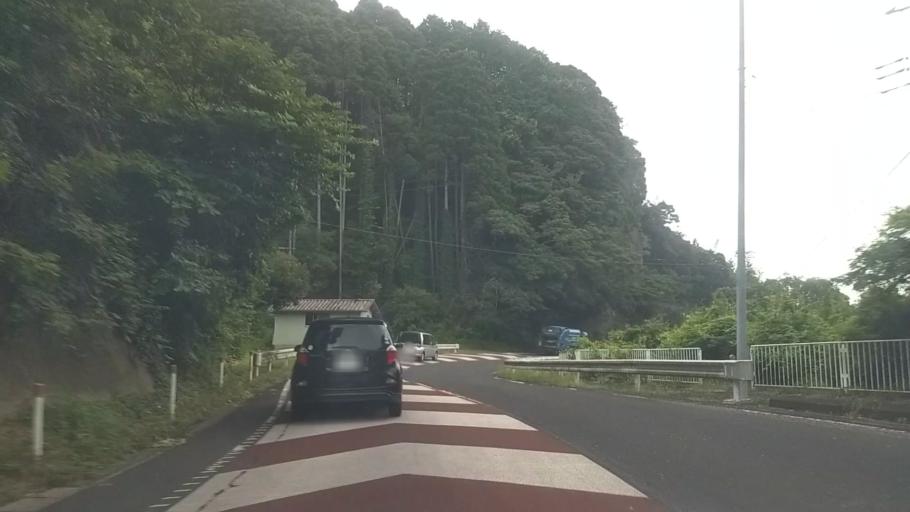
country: JP
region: Chiba
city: Ohara
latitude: 35.2658
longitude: 140.3707
